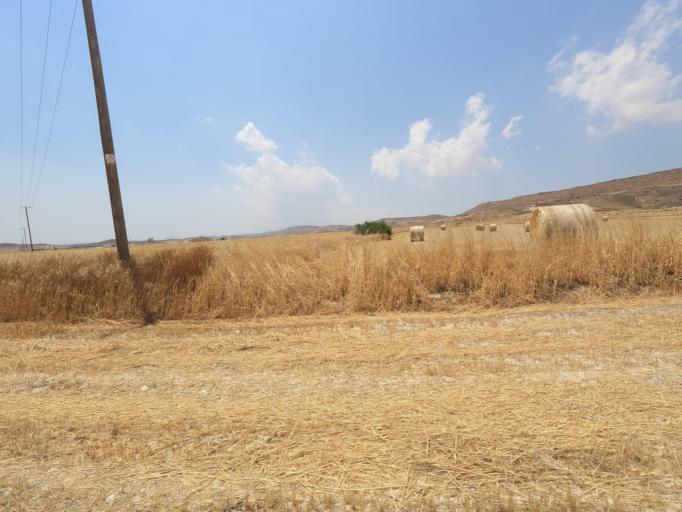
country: CY
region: Larnaka
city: Troulloi
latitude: 35.0381
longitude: 33.6051
